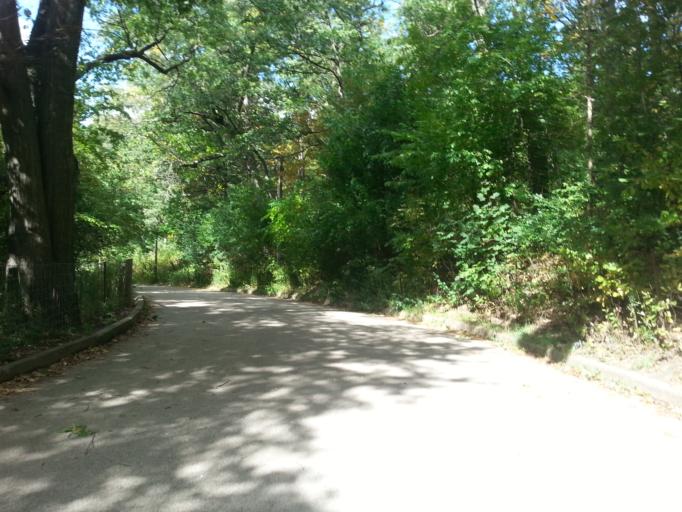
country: CA
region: Ontario
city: Toronto
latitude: 43.6444
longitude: -79.4581
